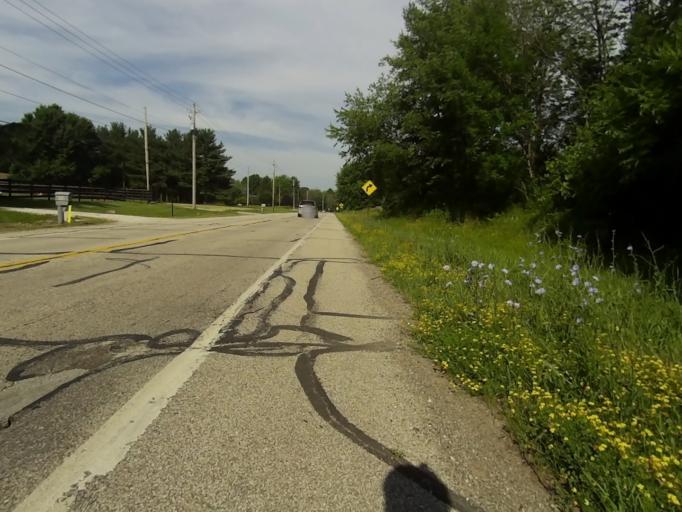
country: US
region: Ohio
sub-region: Summit County
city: Hudson
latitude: 41.2180
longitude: -81.4655
